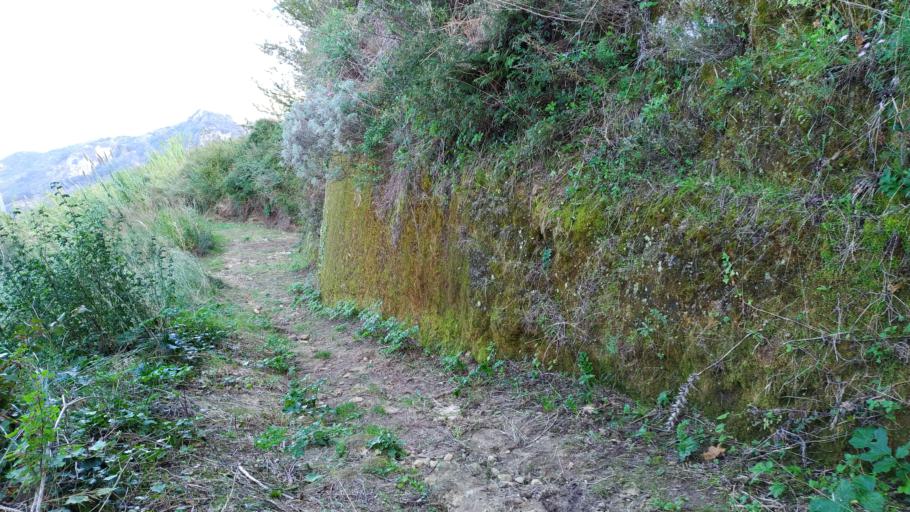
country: IT
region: Sicily
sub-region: Messina
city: Rometta
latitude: 38.1743
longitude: 15.4166
